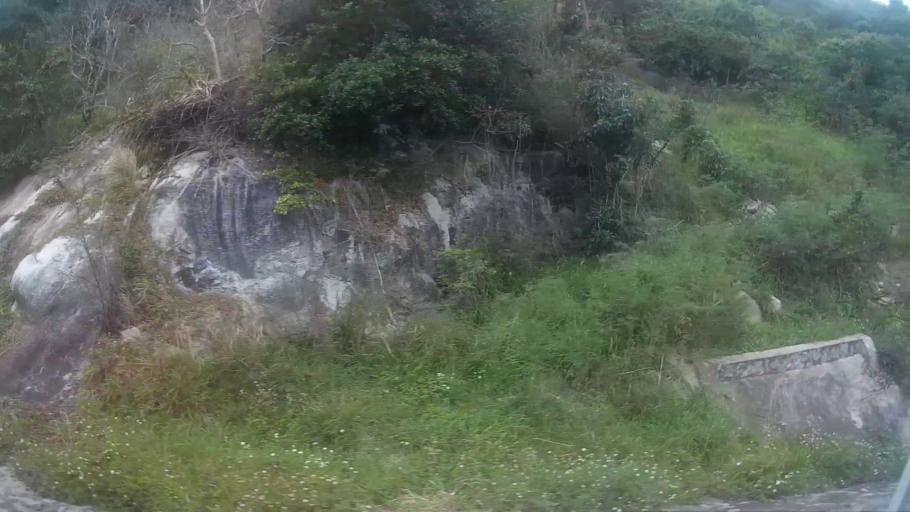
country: VN
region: Khanh Hoa
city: Van Gia
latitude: 12.8608
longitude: 109.4021
